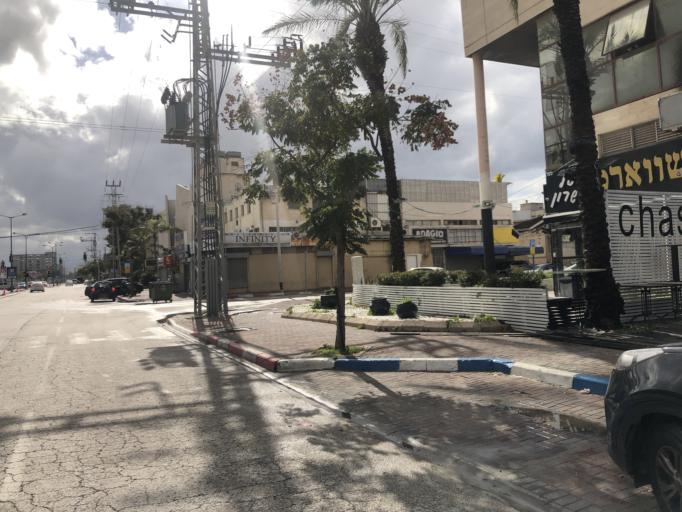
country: IL
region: Central District
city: Bet Yizhaq
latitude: 32.3216
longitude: 34.8743
